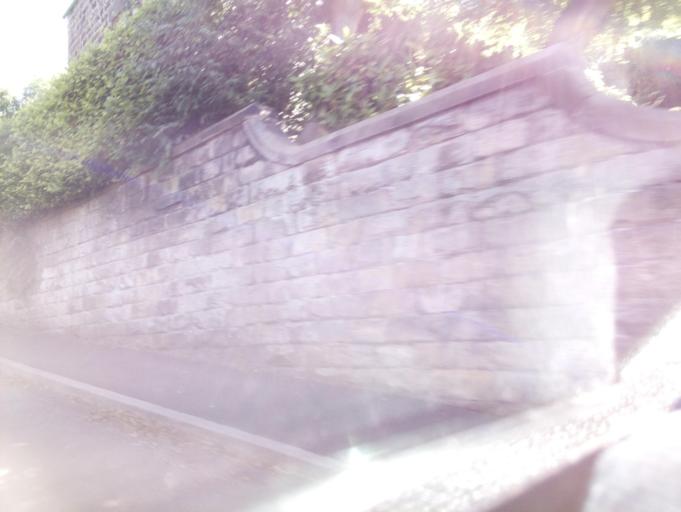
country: GB
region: England
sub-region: Derbyshire
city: Matlock
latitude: 53.1407
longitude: -1.5461
